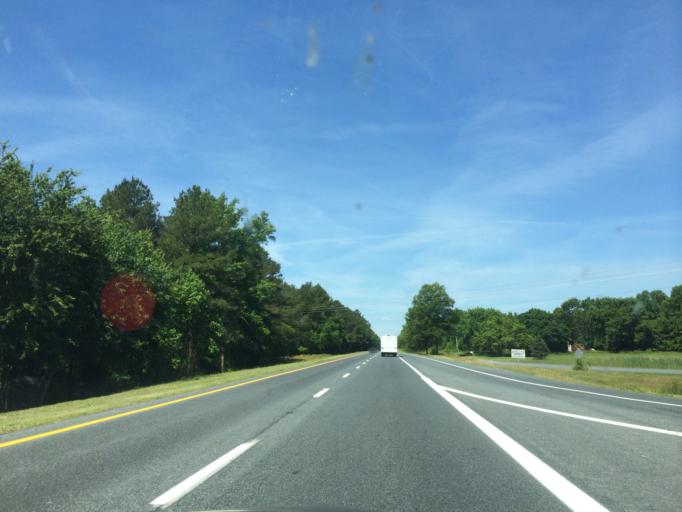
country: US
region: Maryland
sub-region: Wicomico County
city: Pittsville
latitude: 38.3848
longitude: -75.4316
